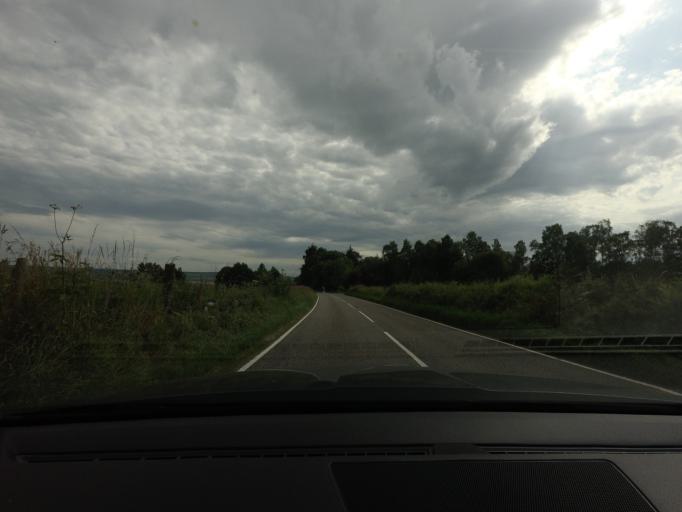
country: GB
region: Scotland
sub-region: Highland
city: Alness
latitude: 57.6993
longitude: -4.2881
